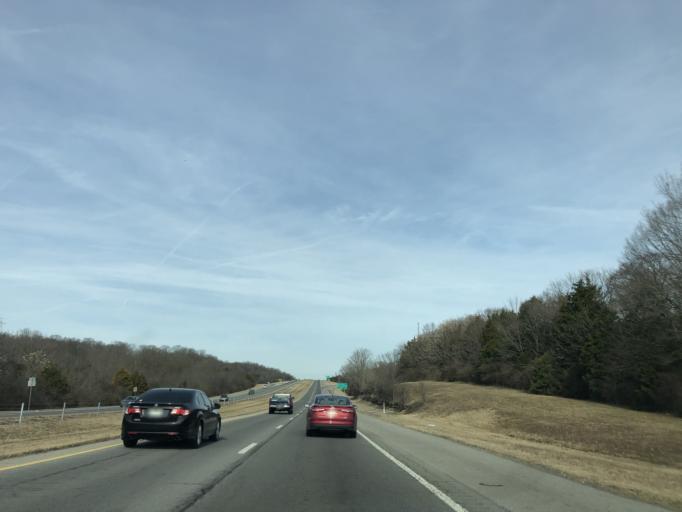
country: US
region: Tennessee
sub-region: Davidson County
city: Nashville
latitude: 36.2116
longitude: -86.7486
